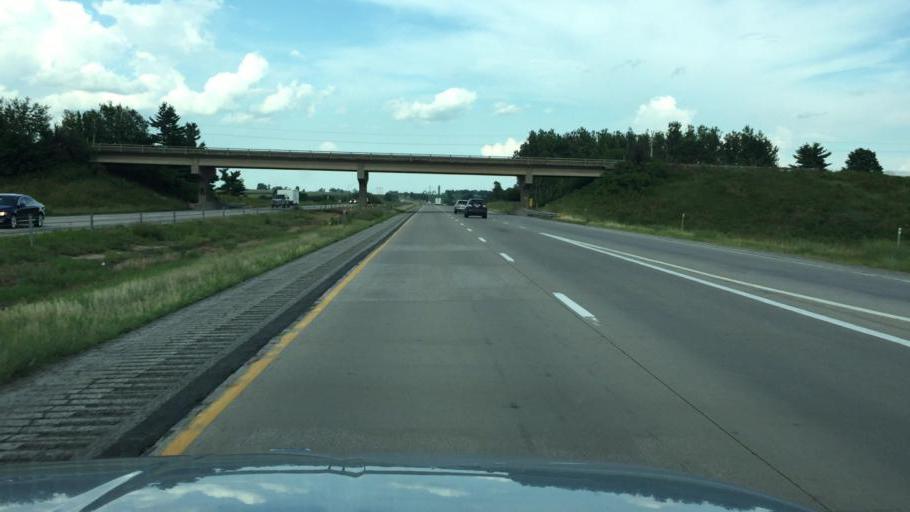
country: US
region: Iowa
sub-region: Iowa County
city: Williamsburg
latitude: 41.6888
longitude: -92.0675
